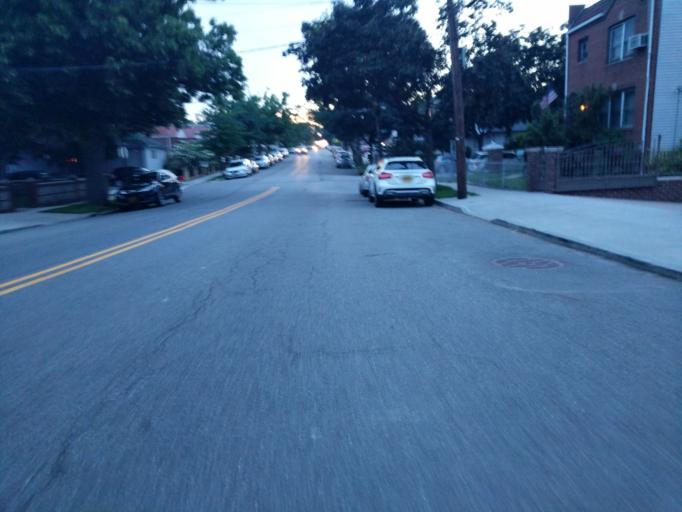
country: US
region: New York
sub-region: Queens County
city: Long Island City
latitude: 40.7709
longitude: -73.8984
